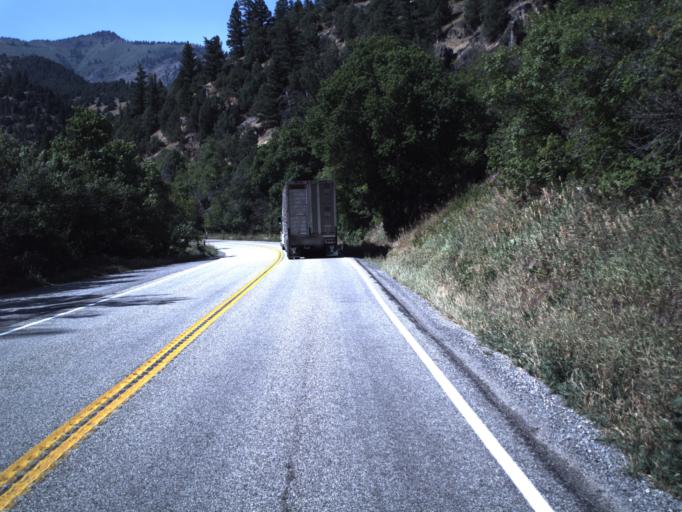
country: US
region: Utah
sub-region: Cache County
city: North Logan
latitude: 41.7859
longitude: -111.6418
